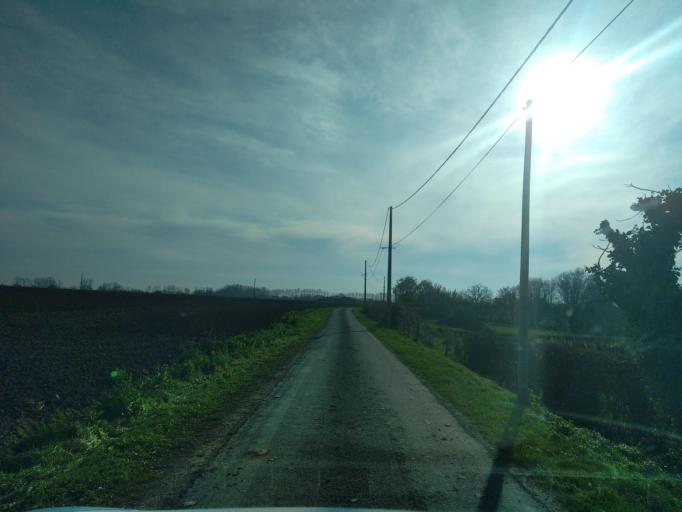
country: FR
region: Pays de la Loire
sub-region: Departement de la Vendee
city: Maillezais
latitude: 46.3523
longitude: -0.7358
